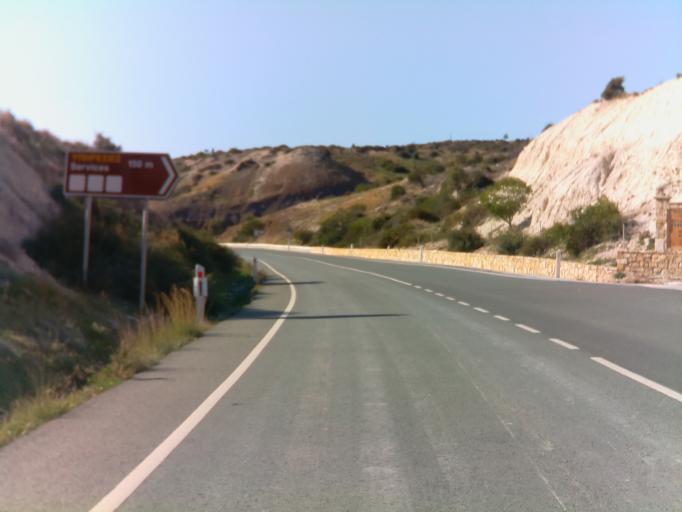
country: CY
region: Limassol
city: Pissouri
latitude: 34.6656
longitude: 32.6336
